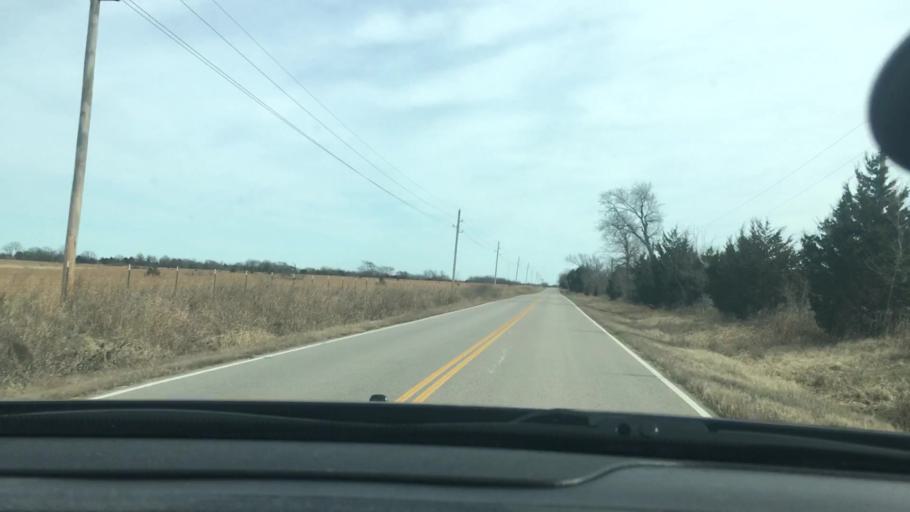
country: US
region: Oklahoma
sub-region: Murray County
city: Sulphur
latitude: 34.4048
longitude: -96.8562
